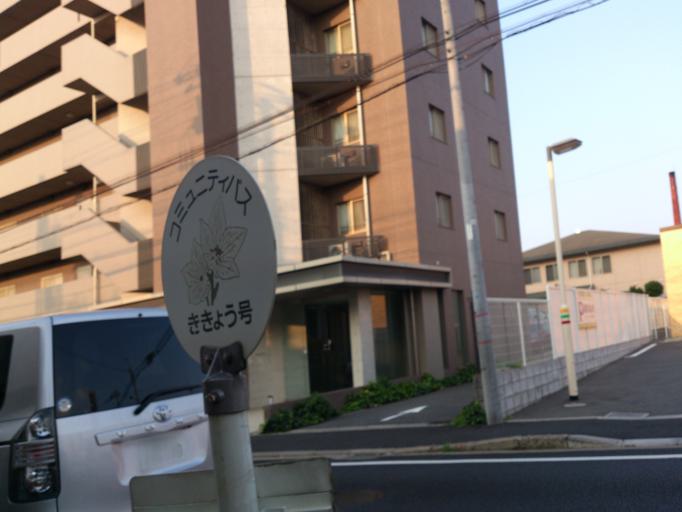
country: JP
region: Chiba
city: Shiroi
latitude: 35.7675
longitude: 139.9984
